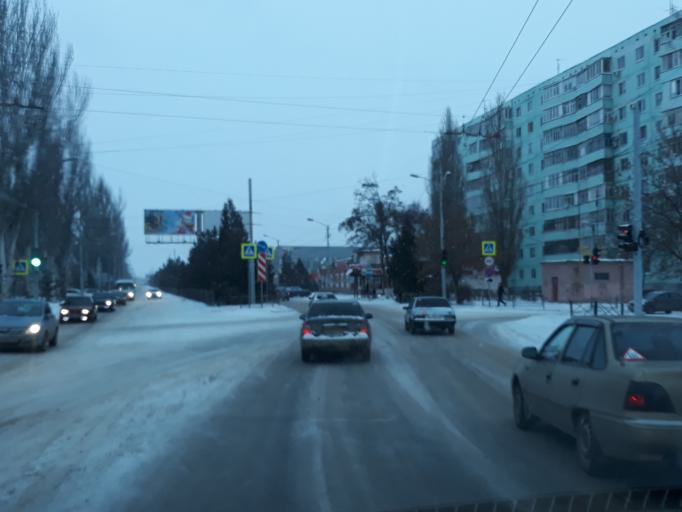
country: RU
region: Rostov
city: Taganrog
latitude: 47.2672
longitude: 38.9236
